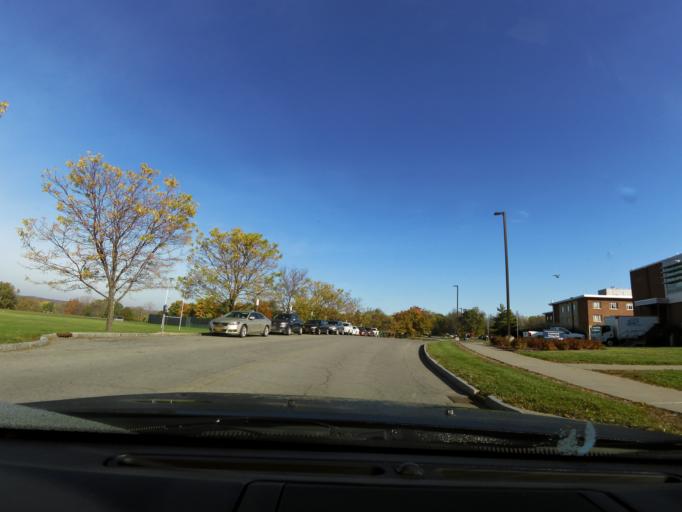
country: US
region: New York
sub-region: Livingston County
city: Geneseo
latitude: 42.7999
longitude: -77.8232
